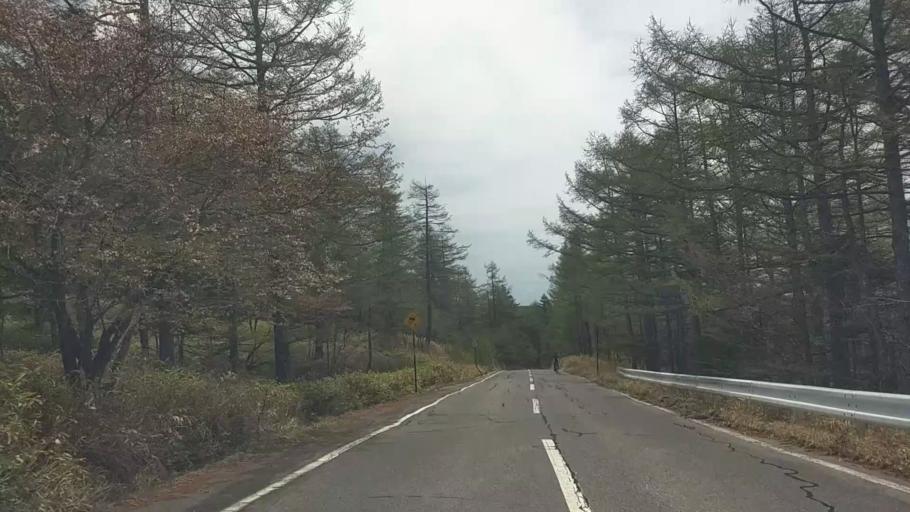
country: JP
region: Nagano
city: Chino
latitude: 36.0532
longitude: 138.3200
